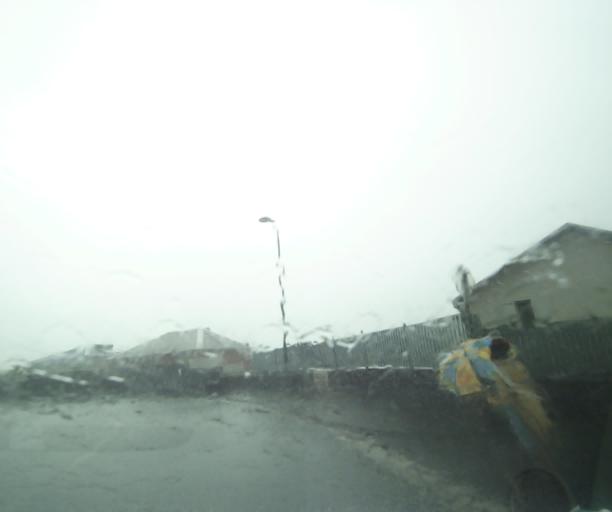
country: RE
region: Reunion
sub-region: Reunion
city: La Possession
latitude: -20.9896
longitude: 55.3292
